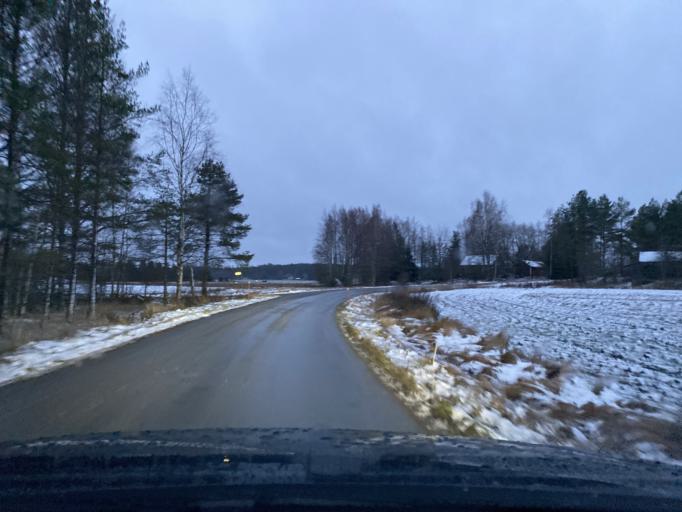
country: FI
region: Pirkanmaa
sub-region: Lounais-Pirkanmaa
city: Punkalaidun
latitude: 61.1420
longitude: 22.9654
